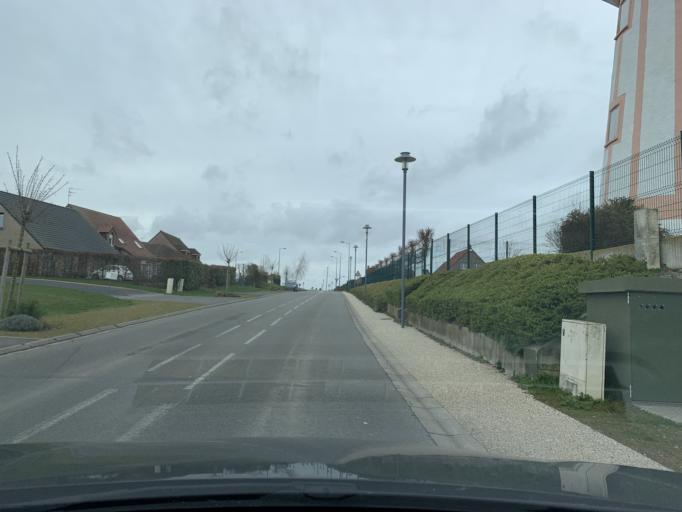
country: FR
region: Nord-Pas-de-Calais
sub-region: Departement du Nord
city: Cambrai
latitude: 50.1546
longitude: 3.2740
